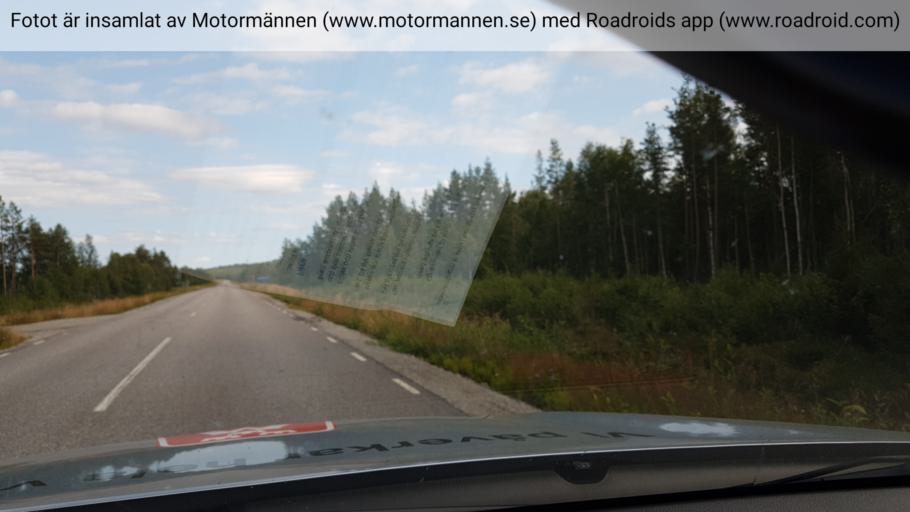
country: SE
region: Vaesterbotten
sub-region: Skelleftea Kommun
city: Boliden
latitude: 65.3148
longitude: 20.2598
